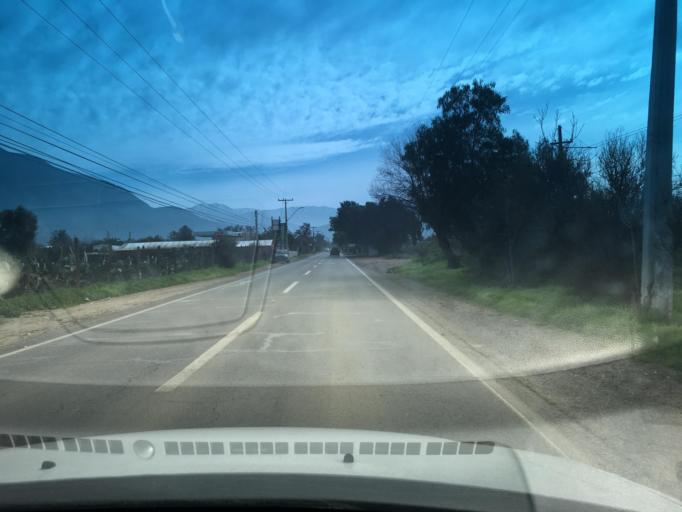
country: CL
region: Santiago Metropolitan
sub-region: Provincia de Chacabuco
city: Lampa
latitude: -33.0979
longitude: -70.9295
